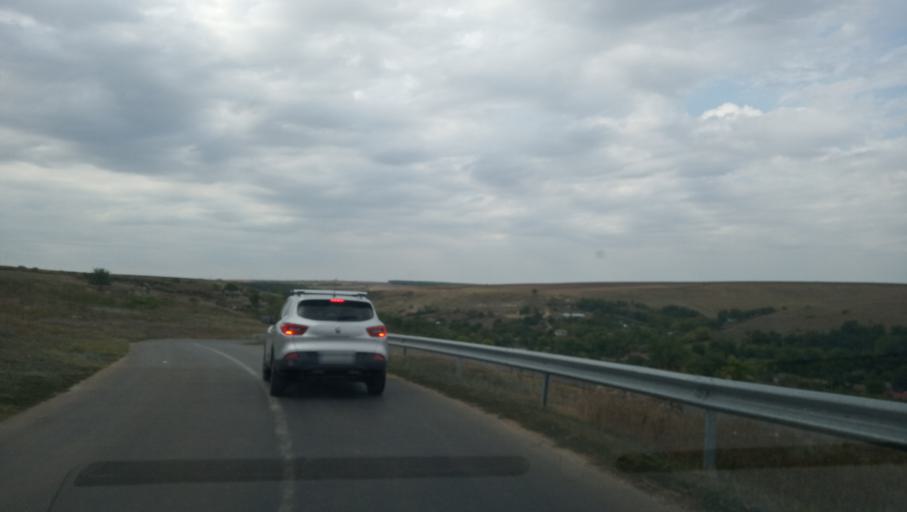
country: RO
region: Constanta
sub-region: Comuna Dumbraveni
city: Dumbraveni
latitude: 43.9888
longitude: 28.0075
